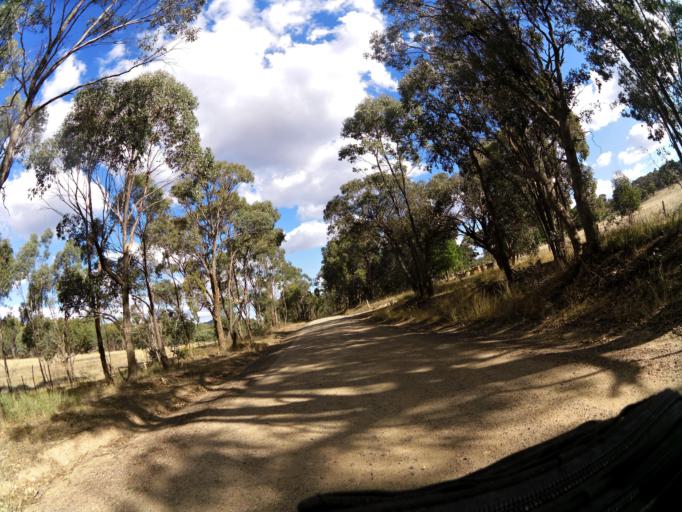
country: AU
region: Victoria
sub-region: Greater Bendigo
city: Kennington
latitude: -36.9974
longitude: 144.8124
